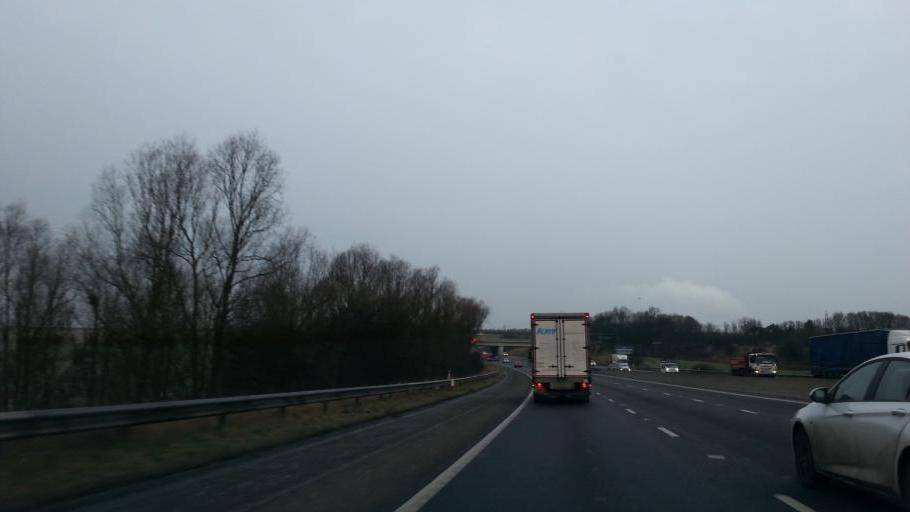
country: GB
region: England
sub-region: Rotherham
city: Ulley
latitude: 53.3925
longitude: -1.2835
